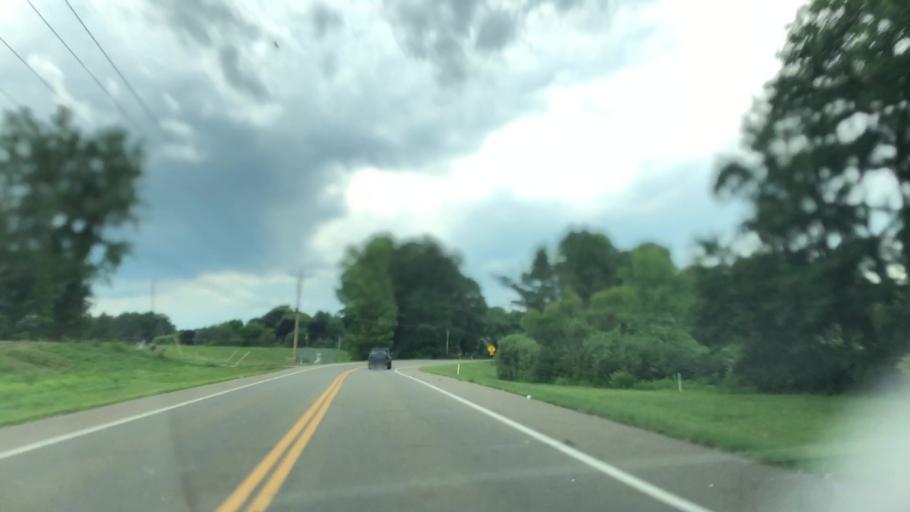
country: US
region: Ohio
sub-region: Summit County
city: New Franklin
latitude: 40.9560
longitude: -81.5276
